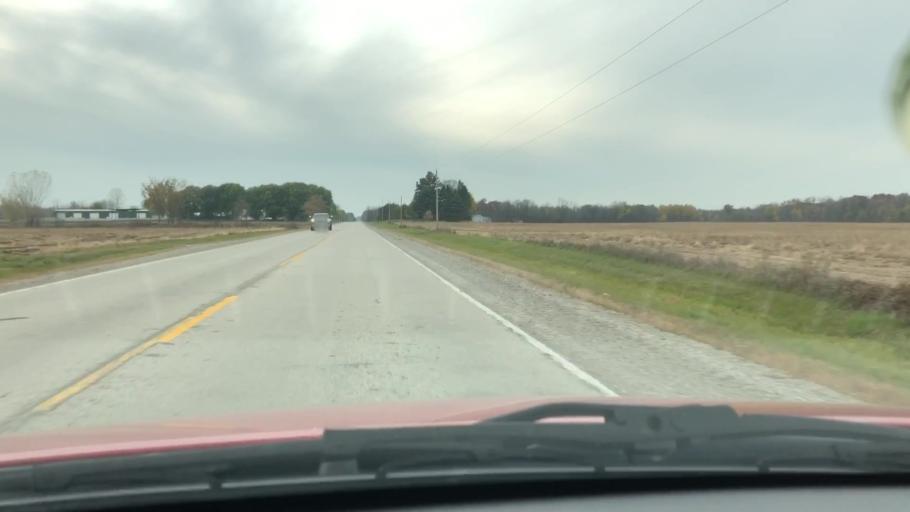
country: US
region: Wisconsin
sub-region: Brown County
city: Oneida
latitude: 44.4442
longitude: -88.1979
